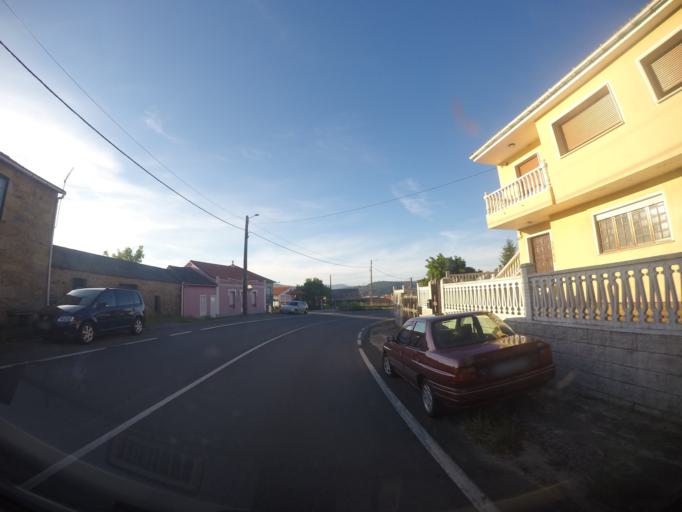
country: ES
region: Galicia
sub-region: Provincia da Coruna
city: Noia
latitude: 42.7789
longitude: -8.9295
